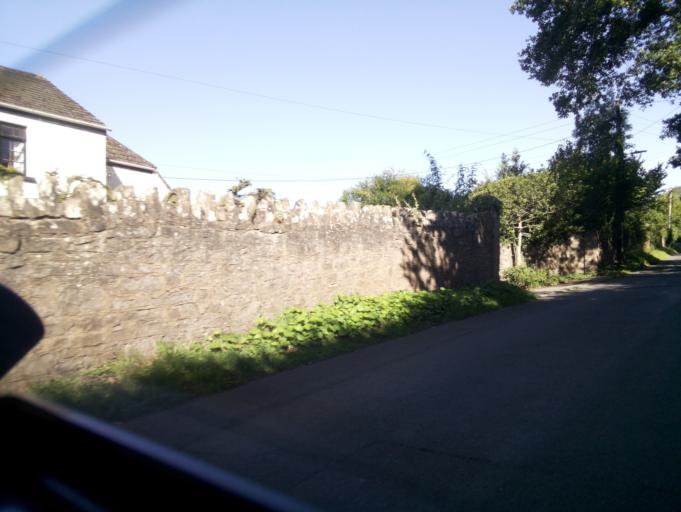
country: GB
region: England
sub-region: Gloucestershire
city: Coleford
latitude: 51.7814
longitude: -2.6461
